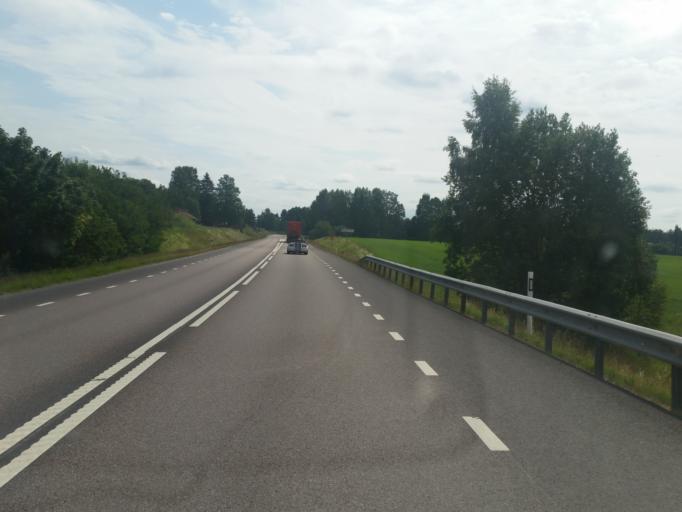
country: SE
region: Dalarna
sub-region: Gagnefs Kommun
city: Gagnef
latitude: 60.6020
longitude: 15.0597
